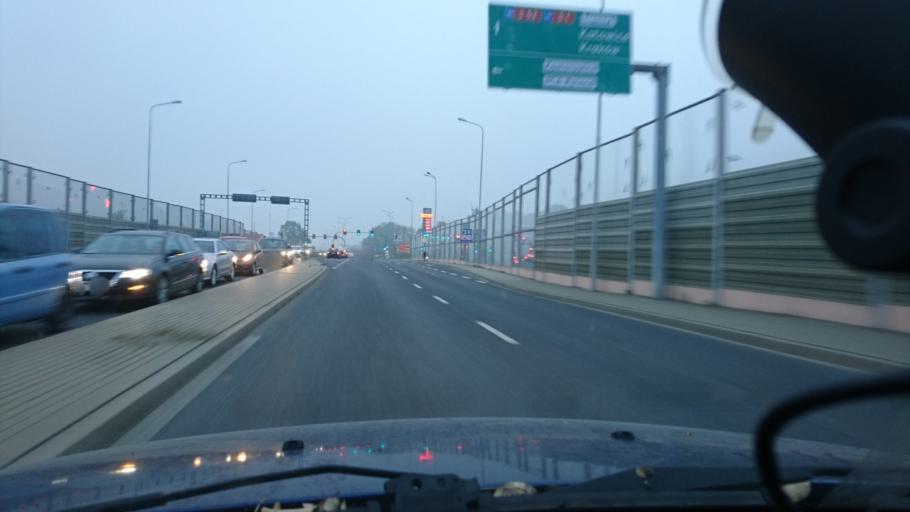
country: PL
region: Silesian Voivodeship
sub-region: Bielsko-Biala
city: Bielsko-Biala
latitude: 49.8376
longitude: 19.0713
